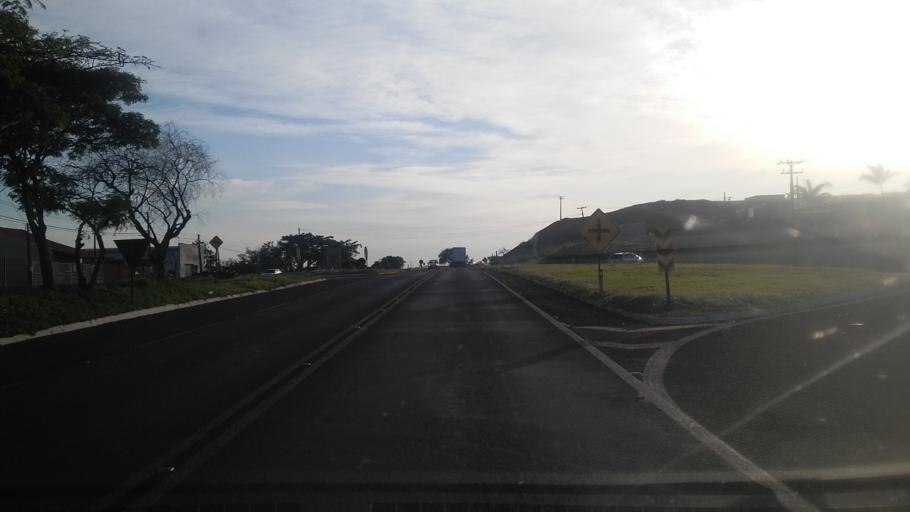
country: BR
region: Parana
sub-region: Bandeirantes
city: Bandeirantes
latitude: -23.1737
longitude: -50.6213
